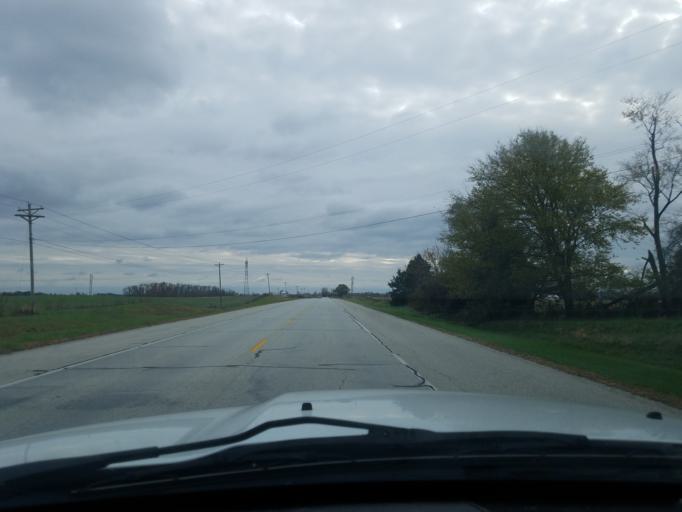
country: US
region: Indiana
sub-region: Bartholomew County
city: Hope
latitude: 39.1929
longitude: -85.7721
